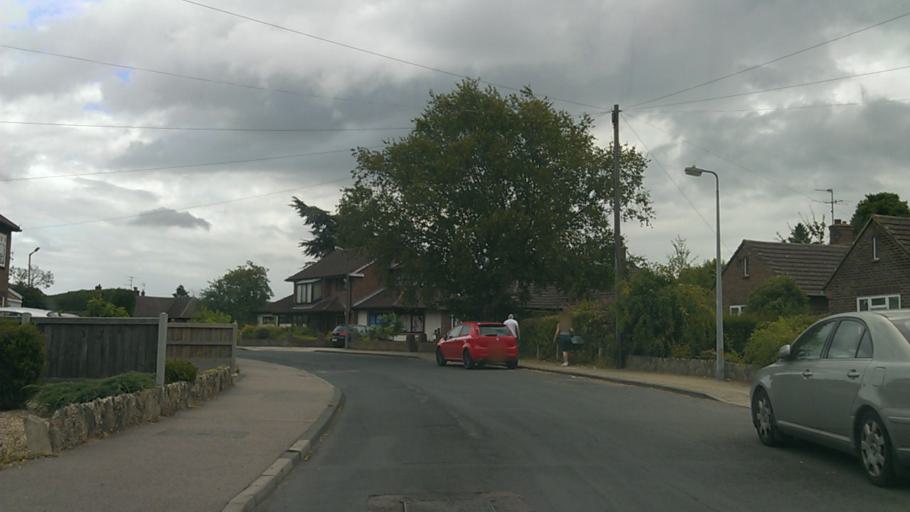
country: GB
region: England
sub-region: Essex
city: West Bergholt
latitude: 51.8804
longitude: 0.8619
